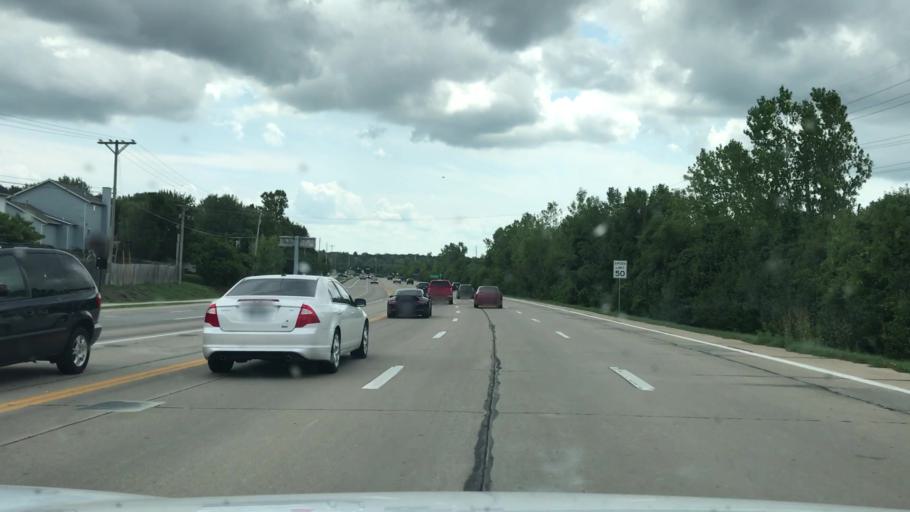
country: US
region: Missouri
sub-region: Saint Charles County
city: Dardenne Prairie
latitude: 38.7504
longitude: -90.7003
